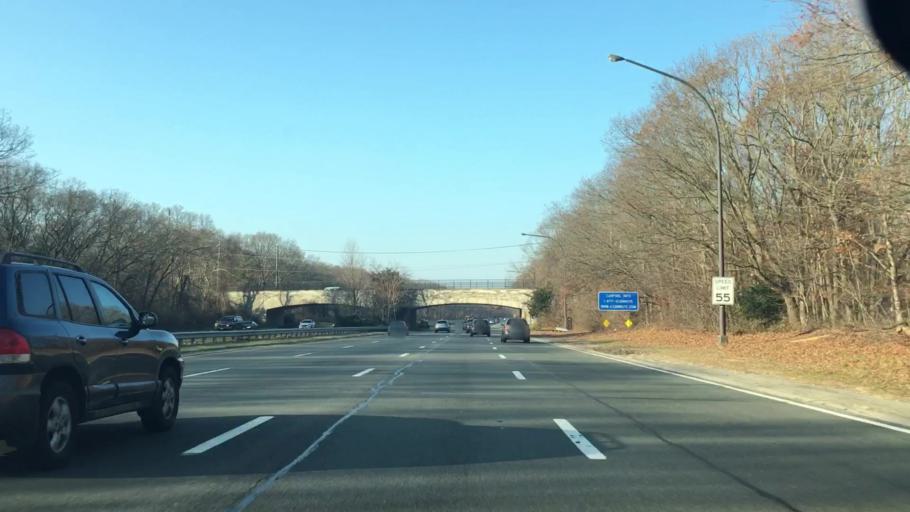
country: US
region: New York
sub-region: Suffolk County
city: Bay Wood
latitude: 40.7340
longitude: -73.2947
